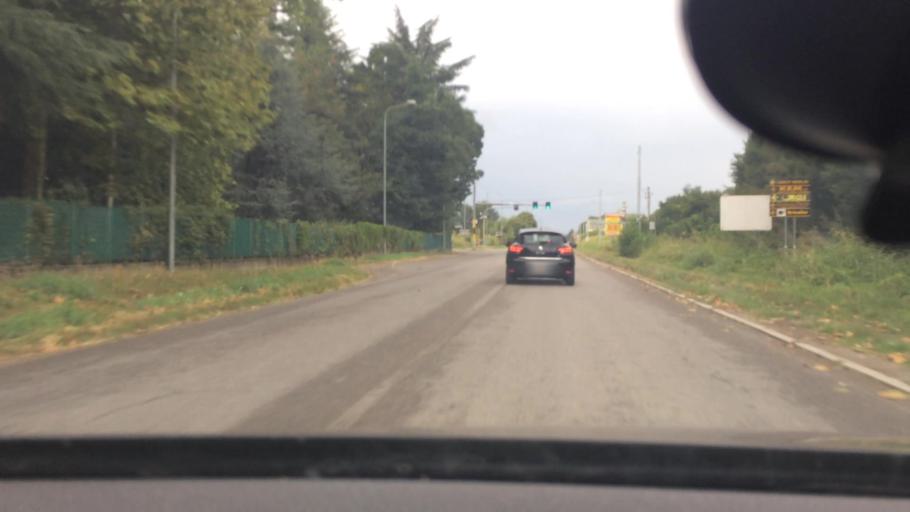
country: IT
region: Lombardy
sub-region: Provincia di Monza e Brianza
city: Nova Milanese
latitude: 45.5722
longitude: 9.1912
